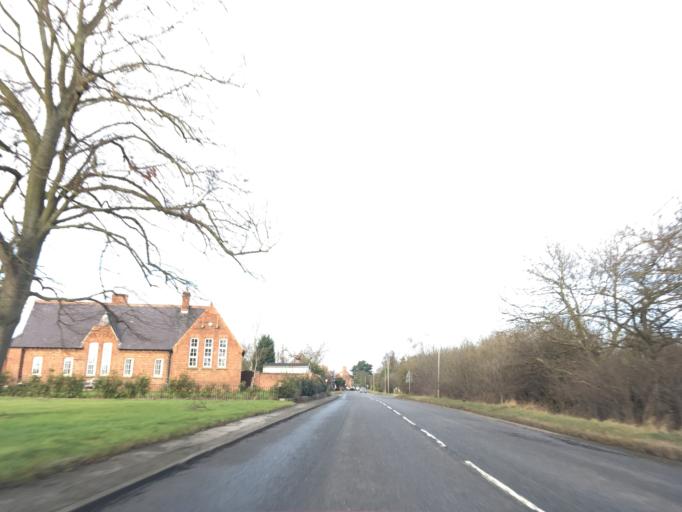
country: GB
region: England
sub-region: Nottinghamshire
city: South Collingham
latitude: 53.1725
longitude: -0.7648
